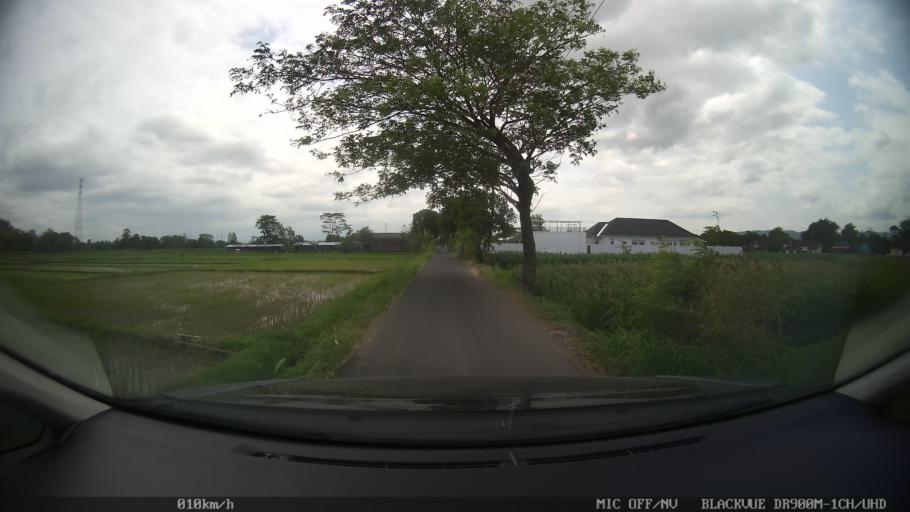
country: ID
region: Daerah Istimewa Yogyakarta
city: Depok
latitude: -7.8235
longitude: 110.4641
